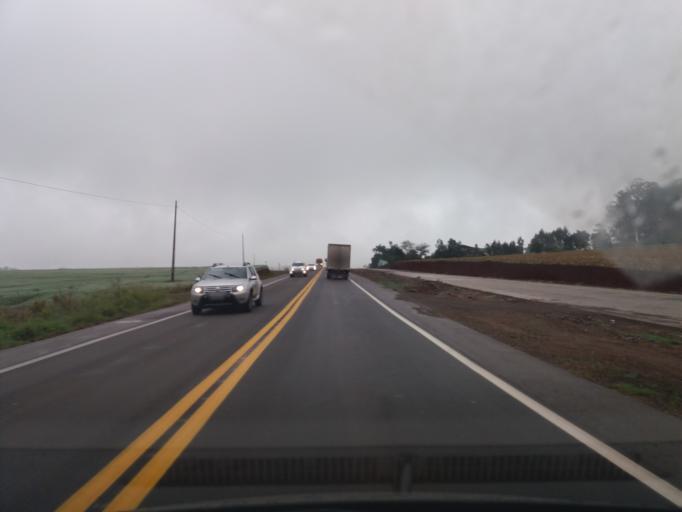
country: BR
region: Parana
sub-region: Realeza
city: Realeza
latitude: -25.4444
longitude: -53.5786
